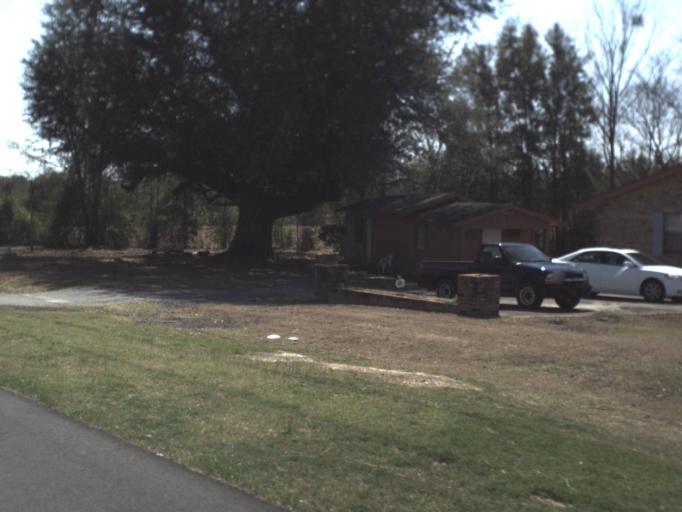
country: US
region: Florida
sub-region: Jackson County
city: Malone
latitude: 30.8475
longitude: -85.0716
